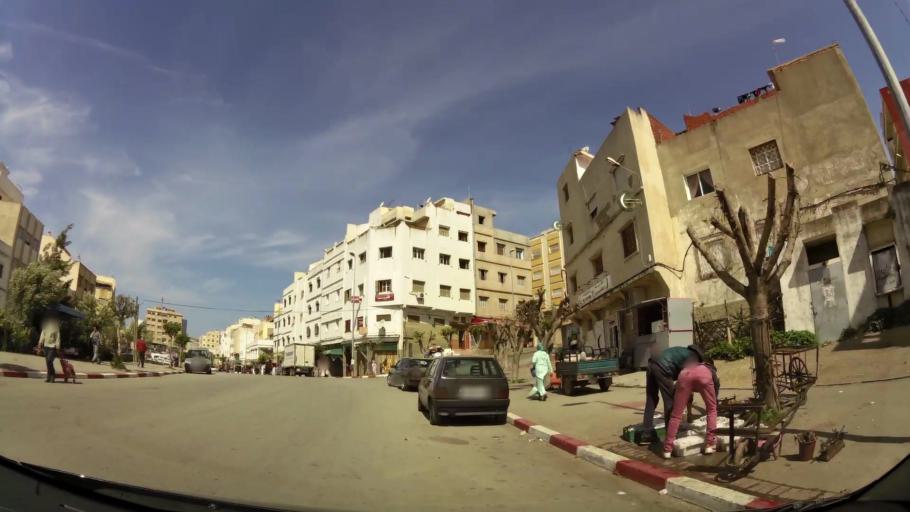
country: MA
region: Tanger-Tetouan
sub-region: Tanger-Assilah
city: Tangier
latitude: 35.7368
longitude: -5.8028
